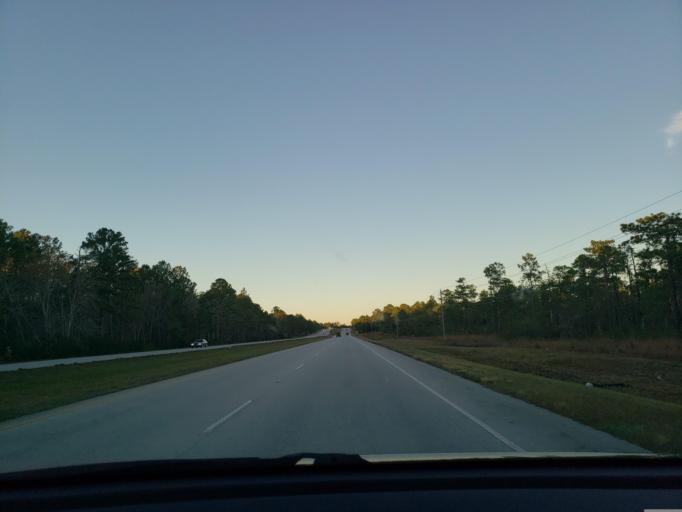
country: US
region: North Carolina
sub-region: Onslow County
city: Sneads Ferry
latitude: 34.6065
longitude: -77.4826
